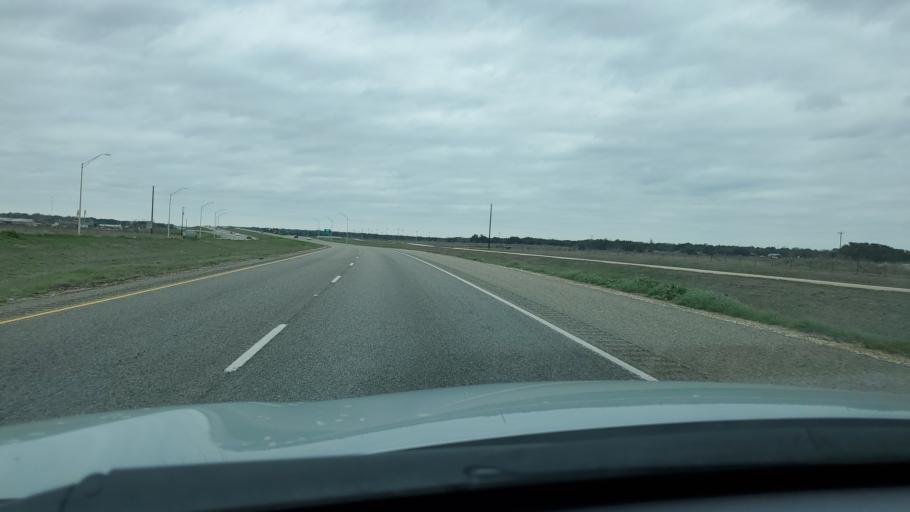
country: US
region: Texas
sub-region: Williamson County
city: Florence
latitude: 30.8361
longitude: -97.7819
